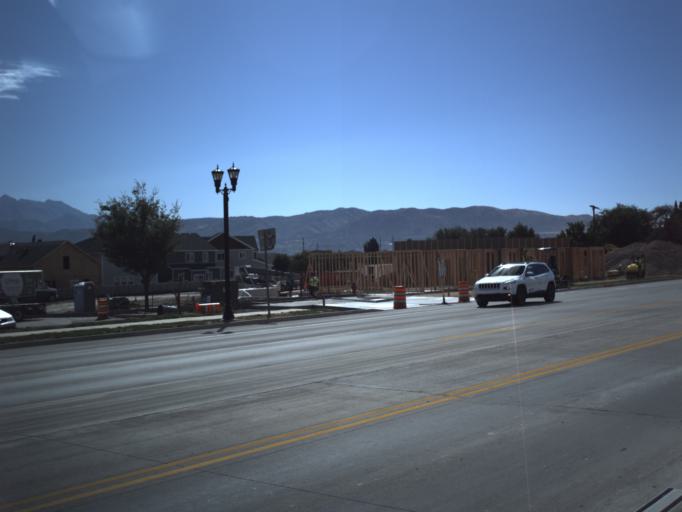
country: US
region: Utah
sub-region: Salt Lake County
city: South Jordan
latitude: 40.5506
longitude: -111.9388
